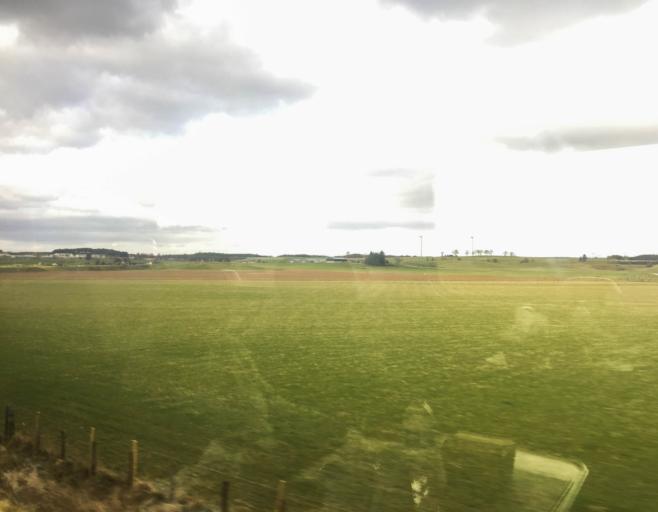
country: GB
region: Scotland
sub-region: South Lanarkshire
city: Carnwath
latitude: 55.6812
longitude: -3.6528
